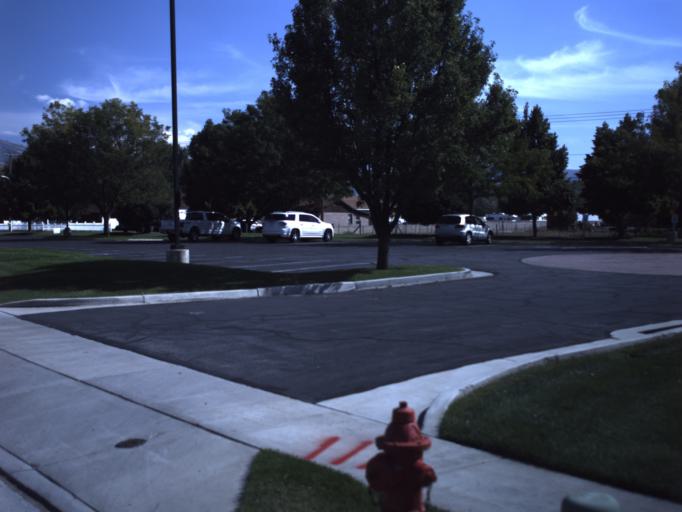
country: US
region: Utah
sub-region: Salt Lake County
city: South Jordan
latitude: 40.5601
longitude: -111.9191
